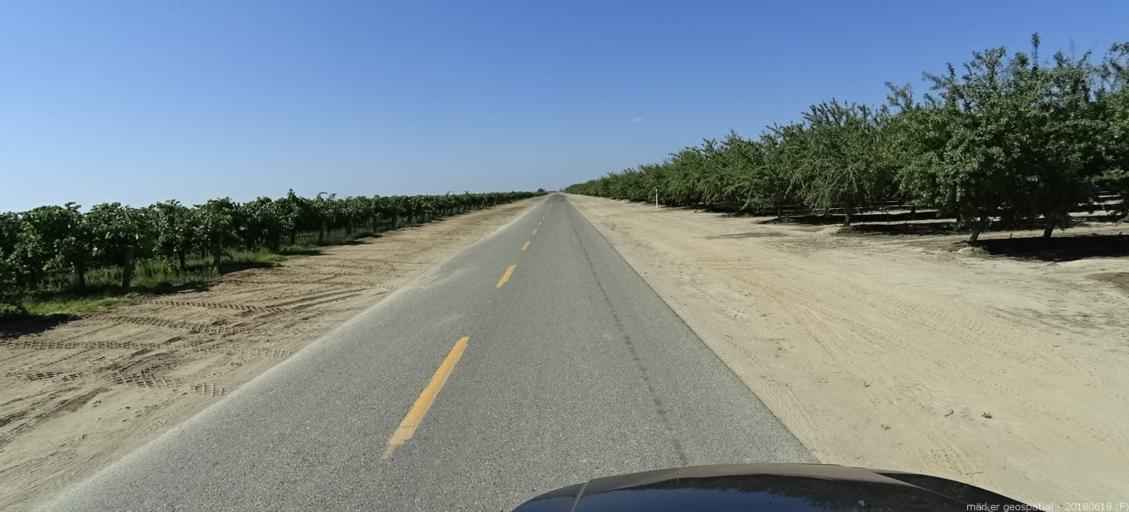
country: US
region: California
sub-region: Madera County
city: Parkwood
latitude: 36.8642
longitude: -120.1465
